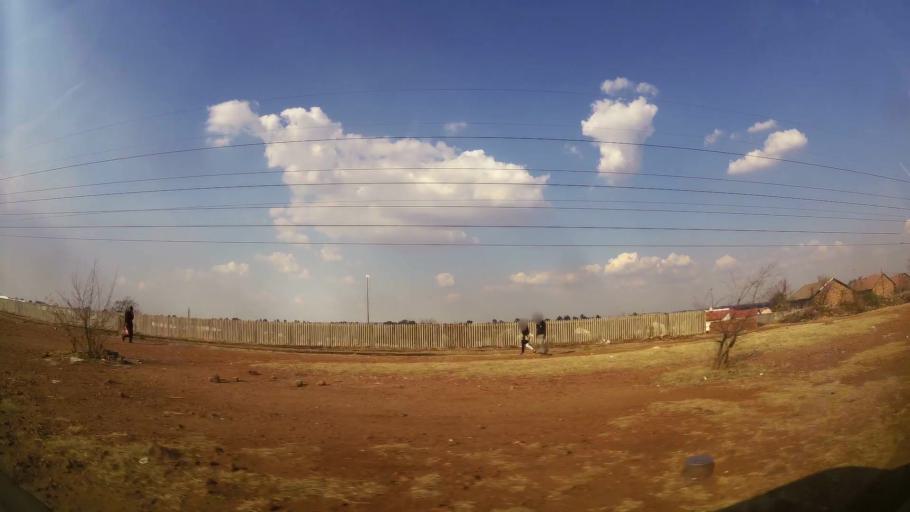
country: ZA
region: Gauteng
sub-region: Ekurhuleni Metropolitan Municipality
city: Germiston
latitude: -26.3568
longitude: 28.2284
